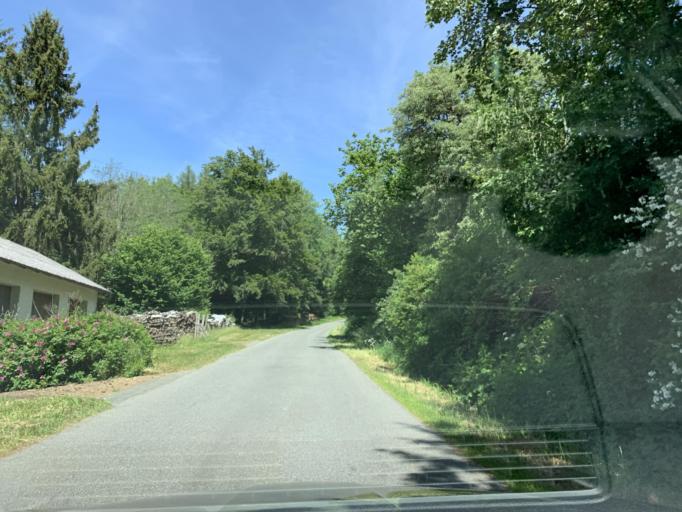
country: DE
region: Bavaria
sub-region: Upper Palatinate
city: Dieterskirchen
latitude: 49.4173
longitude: 12.4373
